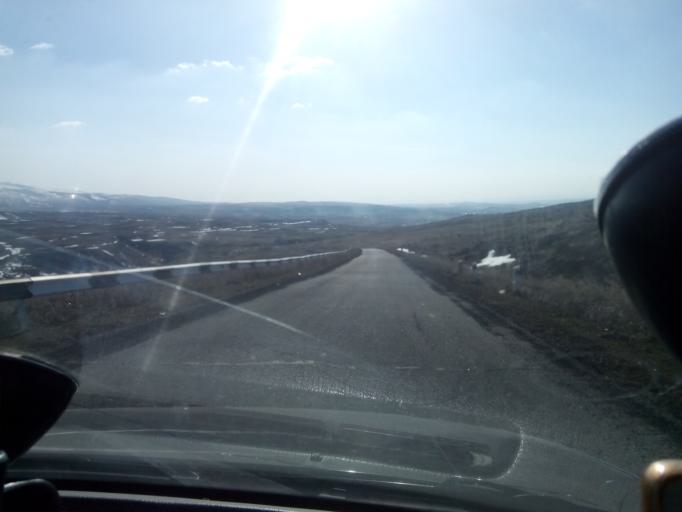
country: AM
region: Kotayk'i Marz
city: Zarr
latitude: 40.2680
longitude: 44.7799
